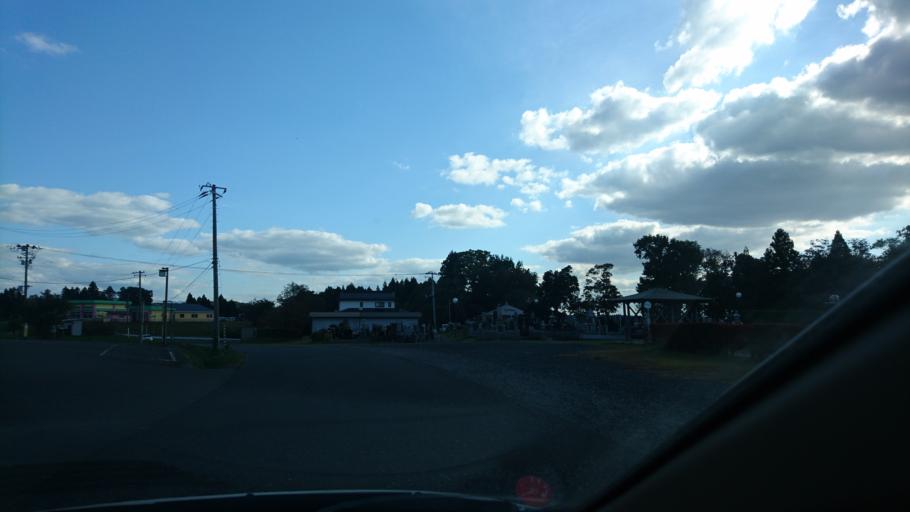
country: JP
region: Iwate
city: Kitakami
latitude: 39.2497
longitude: 141.1246
